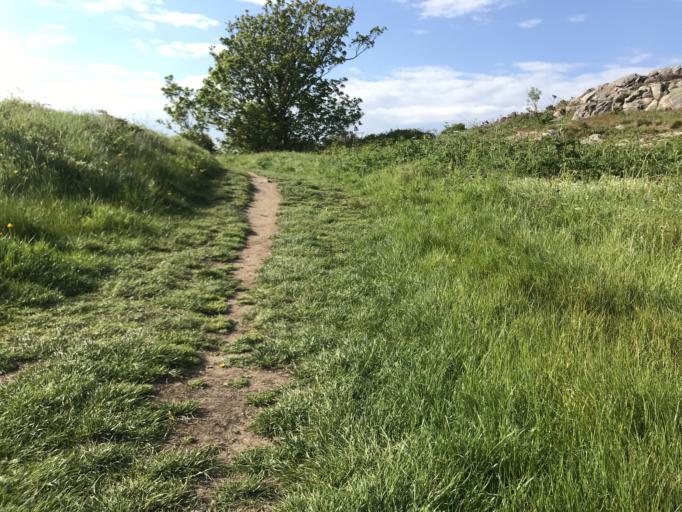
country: IE
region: Leinster
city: Sutton
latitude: 53.3685
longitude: -6.0888
